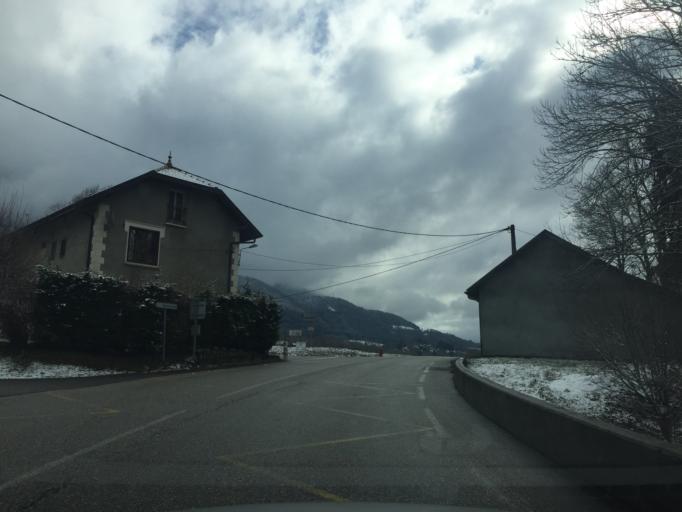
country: FR
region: Rhone-Alpes
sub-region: Departement de la Haute-Savoie
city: Gruffy
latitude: 45.7130
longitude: 6.1134
